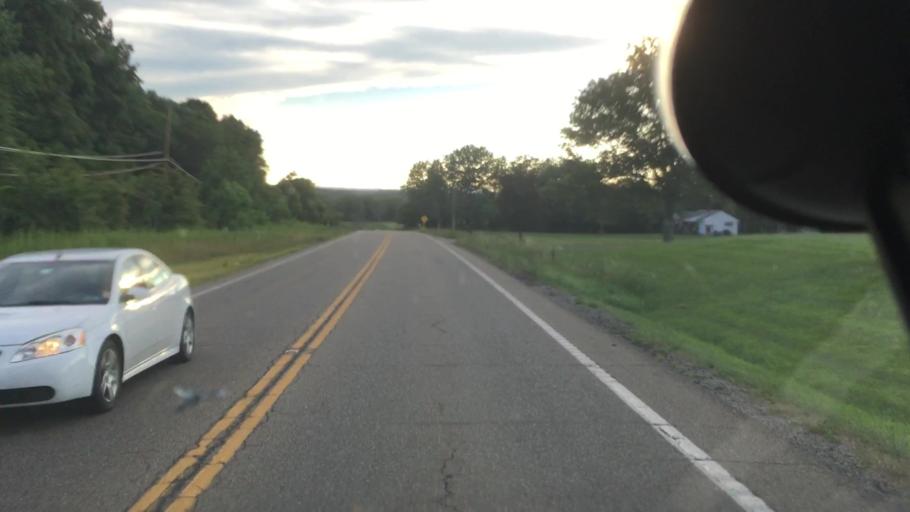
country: US
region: Ohio
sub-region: Columbiana County
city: New Waterford
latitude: 40.8790
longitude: -80.6004
